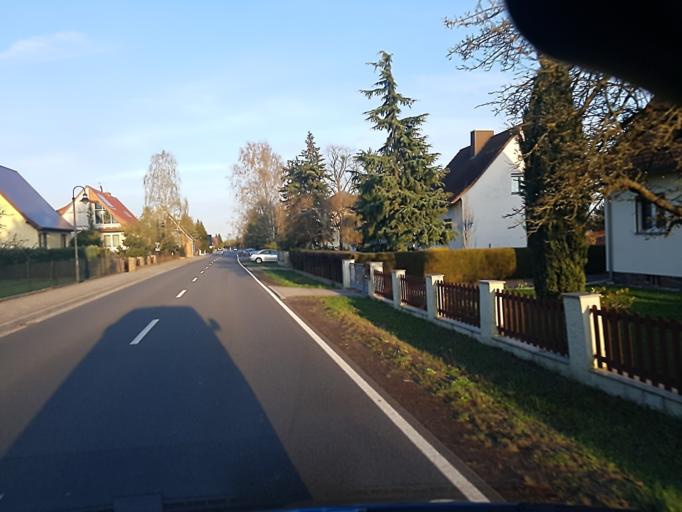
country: DE
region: Saxony
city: Zinna
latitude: 51.5673
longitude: 12.9512
